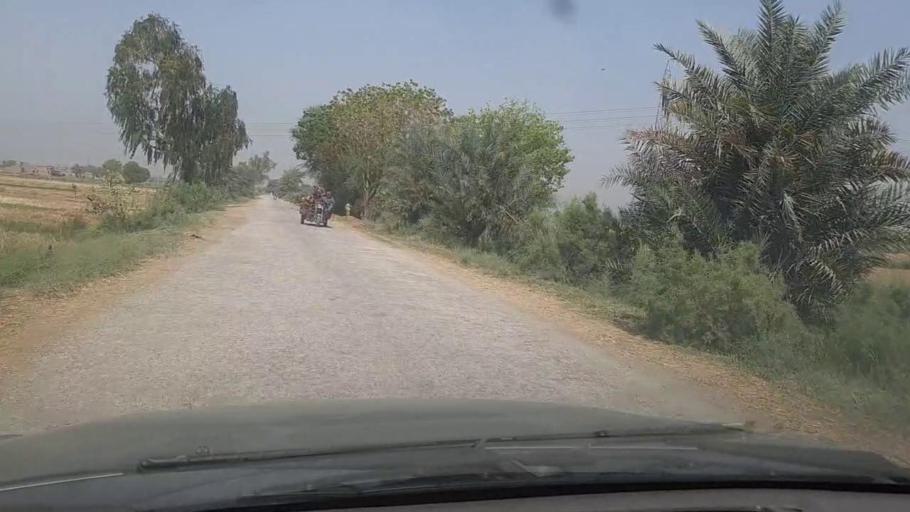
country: PK
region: Sindh
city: Madeji
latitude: 27.7935
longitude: 68.4912
